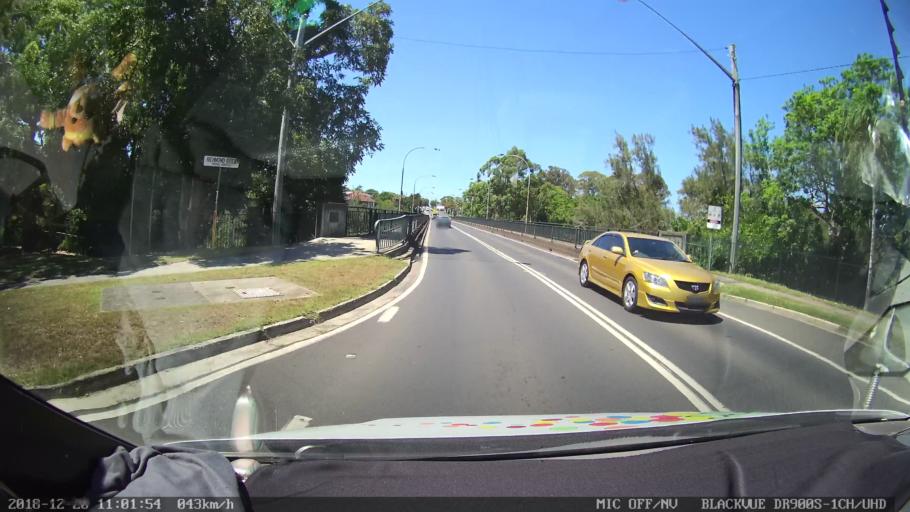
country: AU
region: New South Wales
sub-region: Richmond Valley
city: Casino
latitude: -28.8677
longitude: 153.0449
